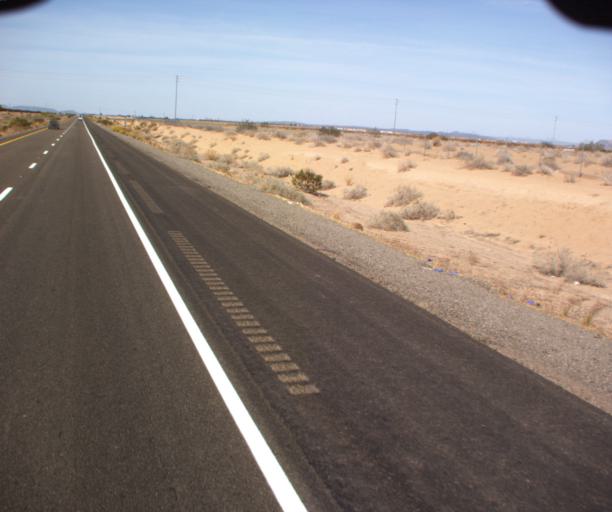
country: US
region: Arizona
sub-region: Yuma County
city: Fortuna Foothills
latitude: 32.6395
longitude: -114.5213
